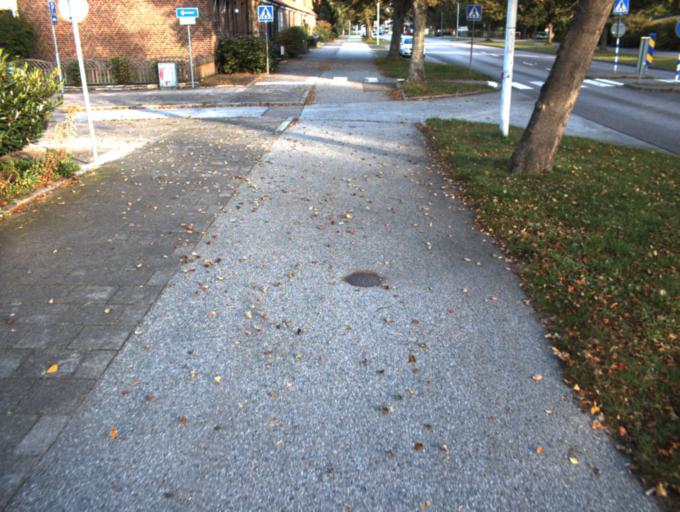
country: SE
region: Skane
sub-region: Helsingborg
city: Helsingborg
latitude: 56.0130
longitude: 12.7260
